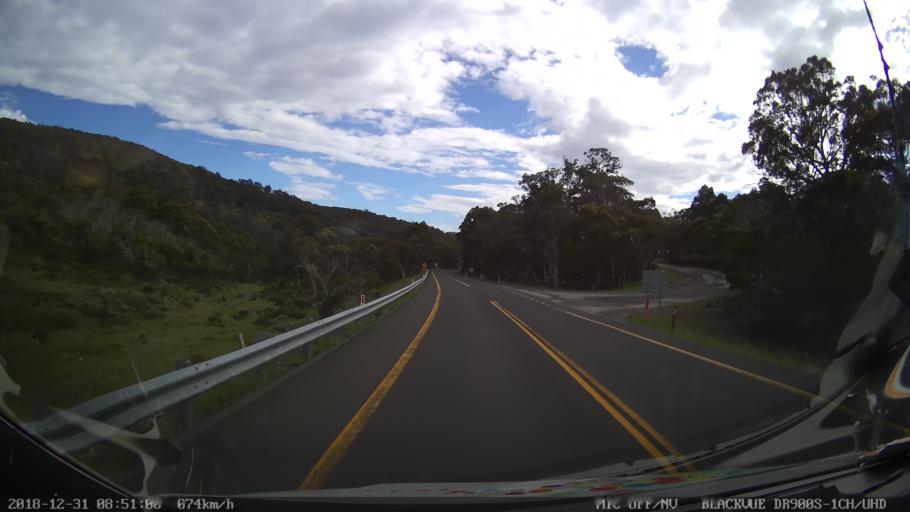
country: AU
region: New South Wales
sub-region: Snowy River
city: Jindabyne
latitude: -36.3495
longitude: 148.5229
